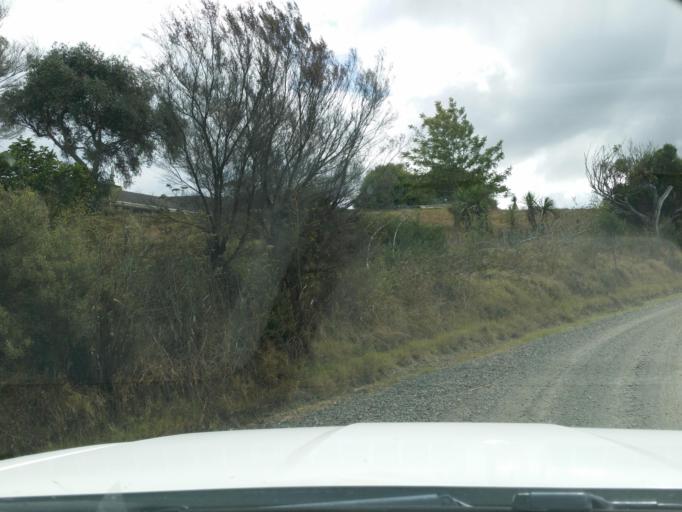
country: NZ
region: Auckland
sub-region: Auckland
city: Wellsford
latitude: -36.3481
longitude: 174.1694
